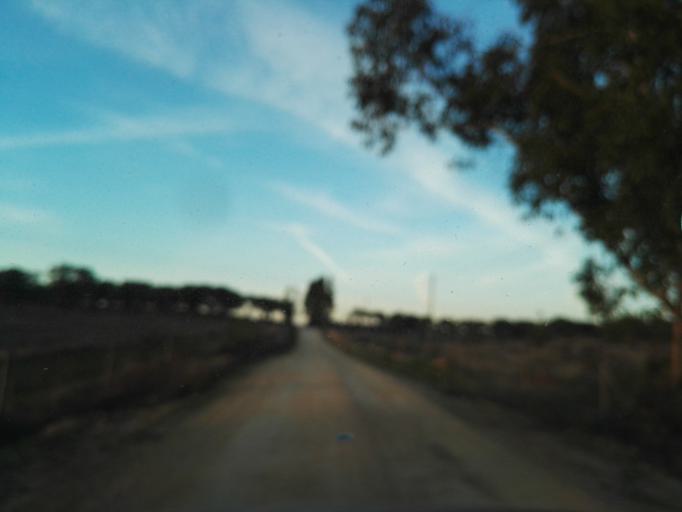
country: PT
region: Evora
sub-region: Montemor-O-Novo
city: Montemor-o-Novo
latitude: 38.7798
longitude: -8.2271
